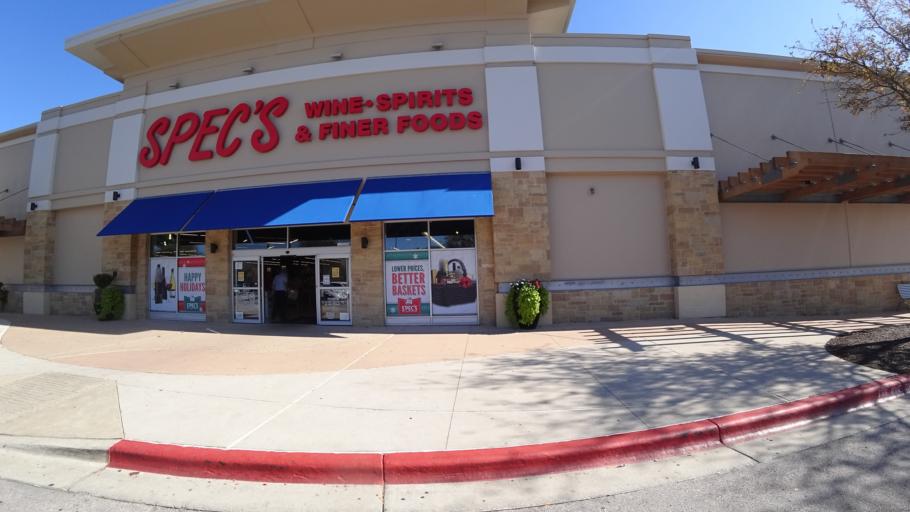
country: US
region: Texas
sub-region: Williamson County
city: Jollyville
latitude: 30.3878
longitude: -97.7335
